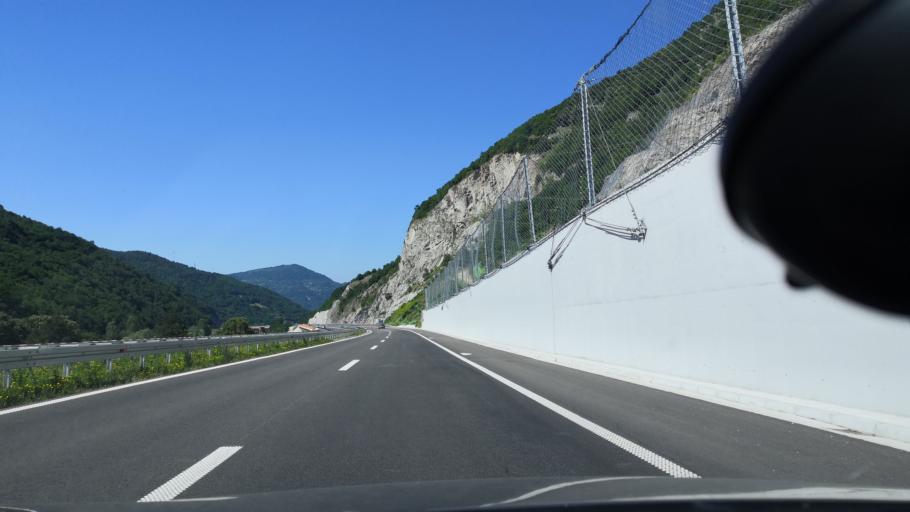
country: RS
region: Central Serbia
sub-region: Pcinjski Okrug
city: Vladicin Han
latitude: 42.7556
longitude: 22.0848
